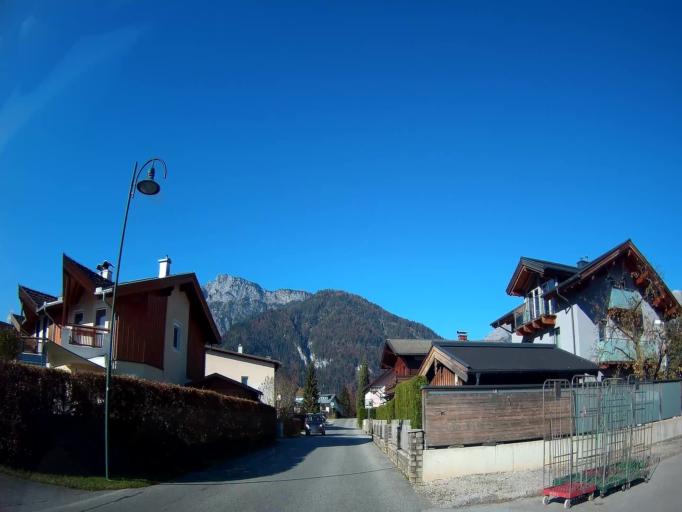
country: AT
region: Salzburg
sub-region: Politischer Bezirk Zell am See
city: Saalfelden am Steinernen Meer
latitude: 47.4401
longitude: 12.8194
